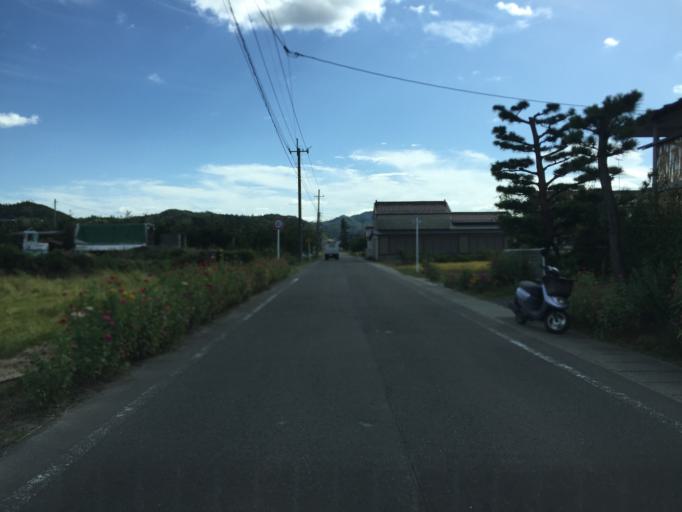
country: JP
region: Fukushima
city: Hobaramachi
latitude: 37.8103
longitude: 140.5727
